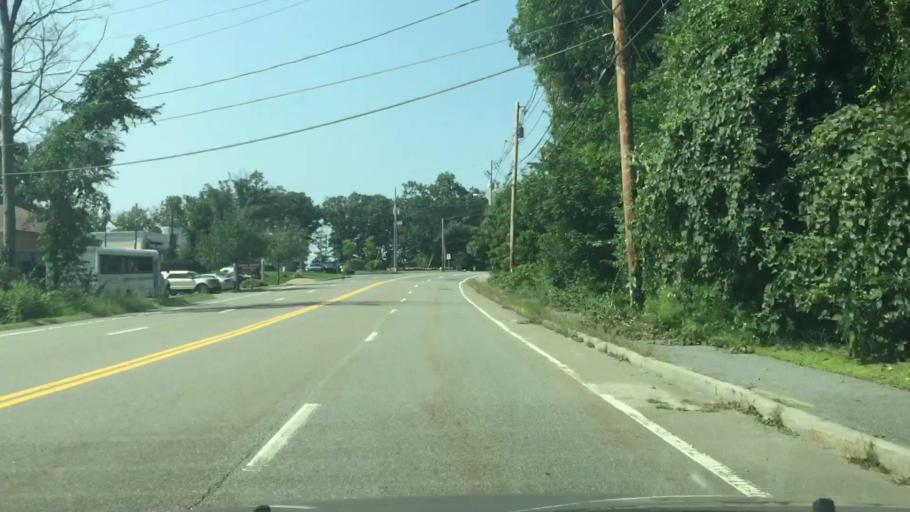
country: US
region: Massachusetts
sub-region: Middlesex County
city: Westford
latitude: 42.5561
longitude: -71.4396
